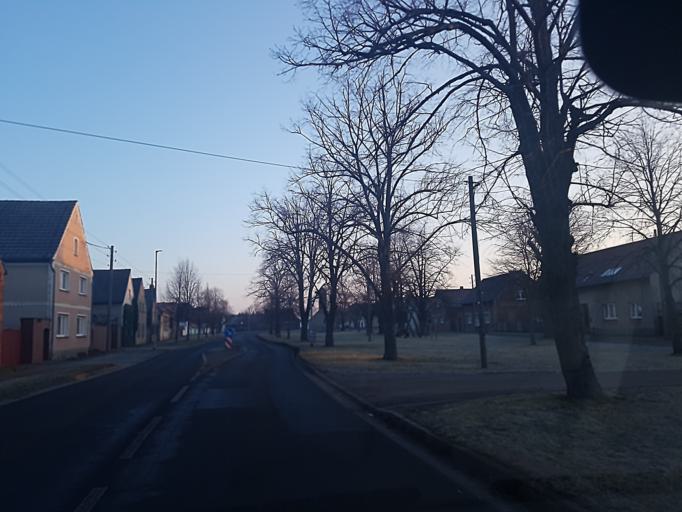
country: DE
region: Saxony-Anhalt
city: Holzdorf
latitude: 51.8175
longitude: 13.1626
